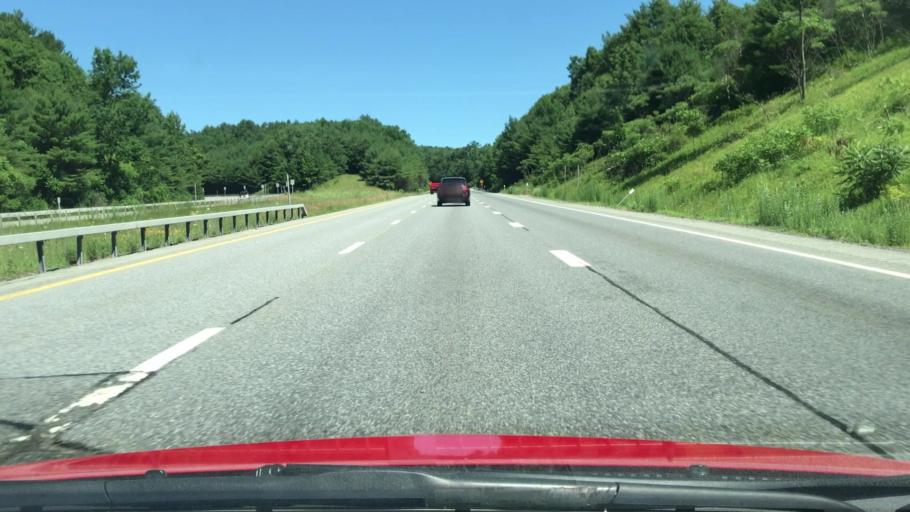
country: US
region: New York
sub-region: Warren County
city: Warrensburg
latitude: 43.4538
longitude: -73.7353
